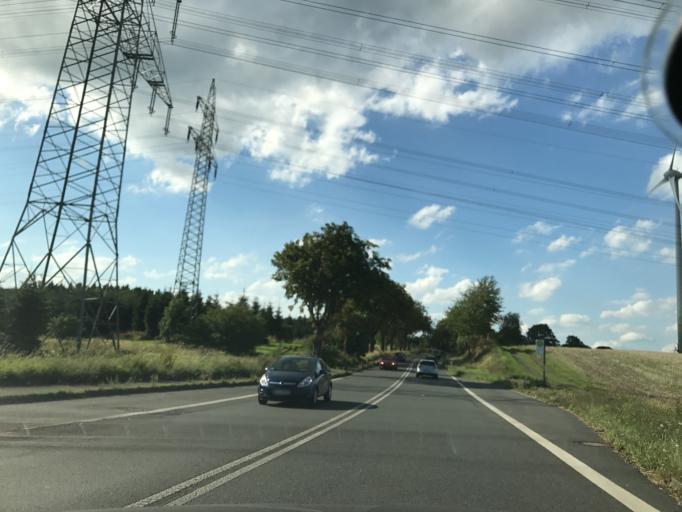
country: DE
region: North Rhine-Westphalia
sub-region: Regierungsbezirk Dusseldorf
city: Velbert
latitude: 51.3598
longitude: 7.0207
